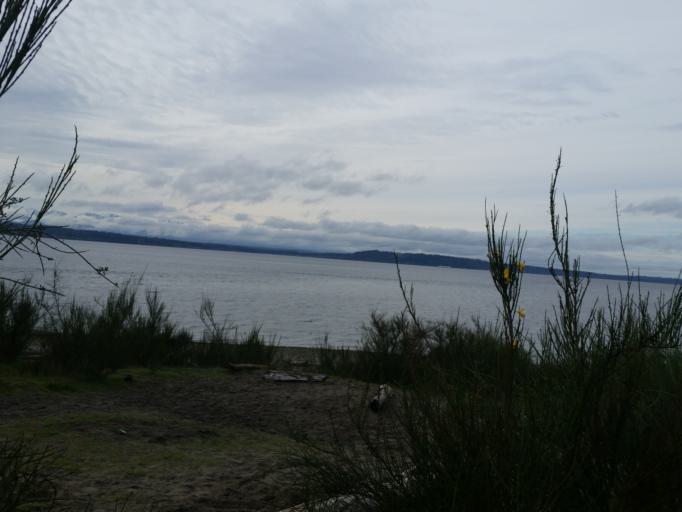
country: US
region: Washington
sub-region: Snohomish County
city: Woodway
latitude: 47.7648
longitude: -122.3865
